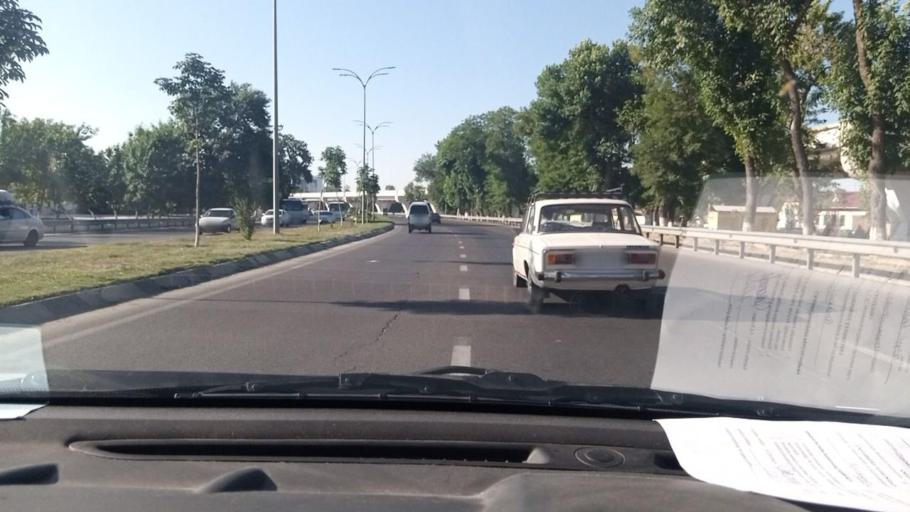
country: UZ
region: Toshkent Shahri
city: Bektemir
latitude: 41.2726
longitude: 69.3622
